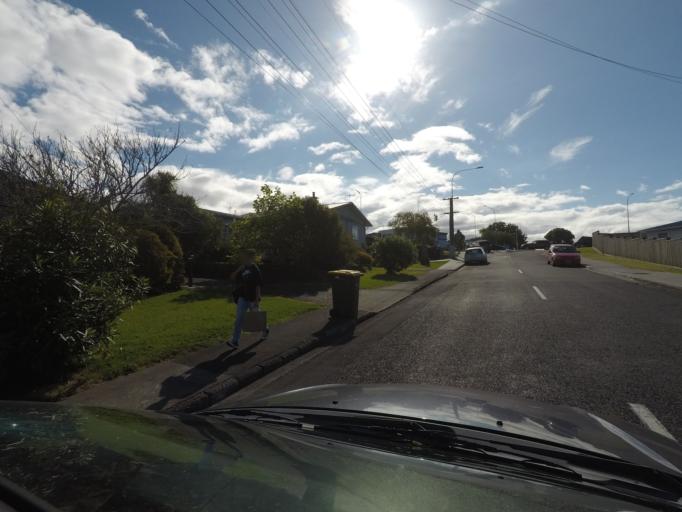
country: NZ
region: Auckland
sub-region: Auckland
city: Rosebank
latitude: -36.8652
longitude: 174.6480
